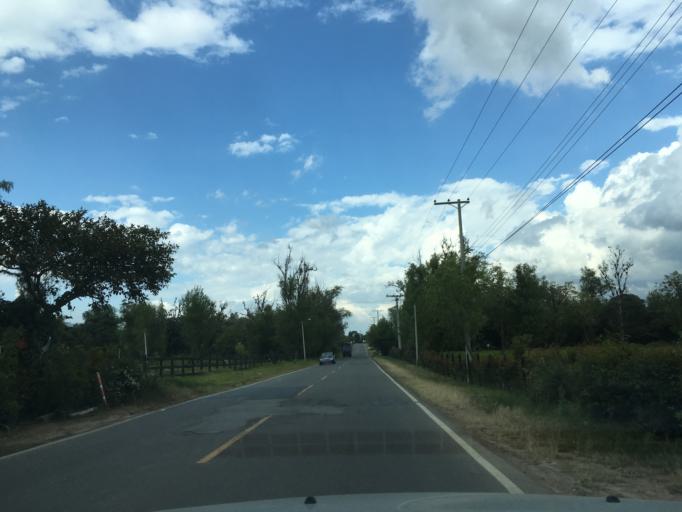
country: CO
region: Boyaca
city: Sutamarchan
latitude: 5.6080
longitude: -73.6323
